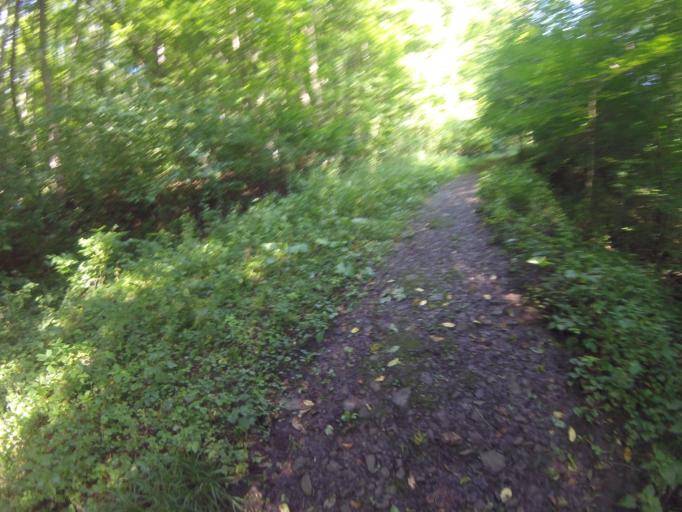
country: SK
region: Nitriansky
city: Sahy
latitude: 47.9835
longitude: 18.8962
